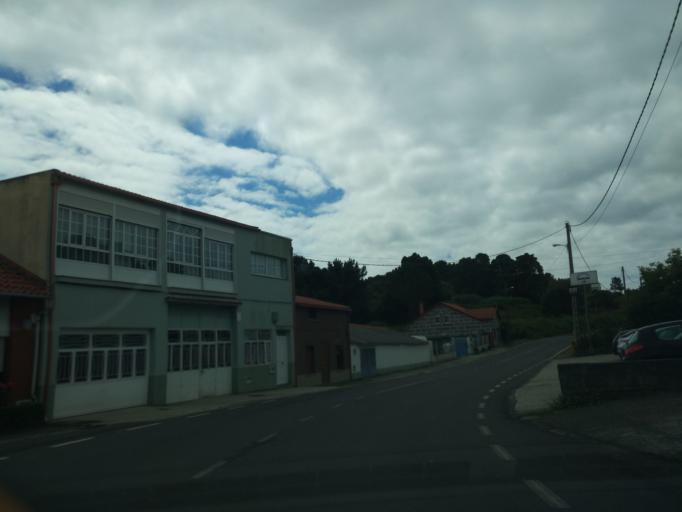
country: ES
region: Galicia
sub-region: Provincia da Coruna
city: Boiro
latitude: 42.6428
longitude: -8.8595
